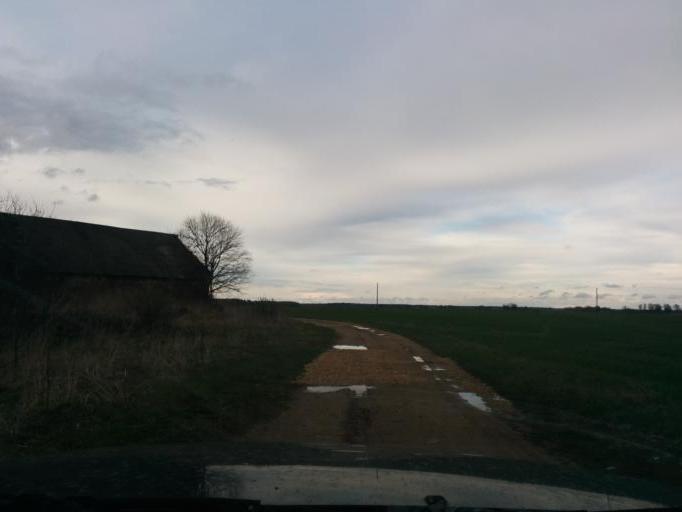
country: LV
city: Tervete
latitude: 56.3655
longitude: 23.5049
